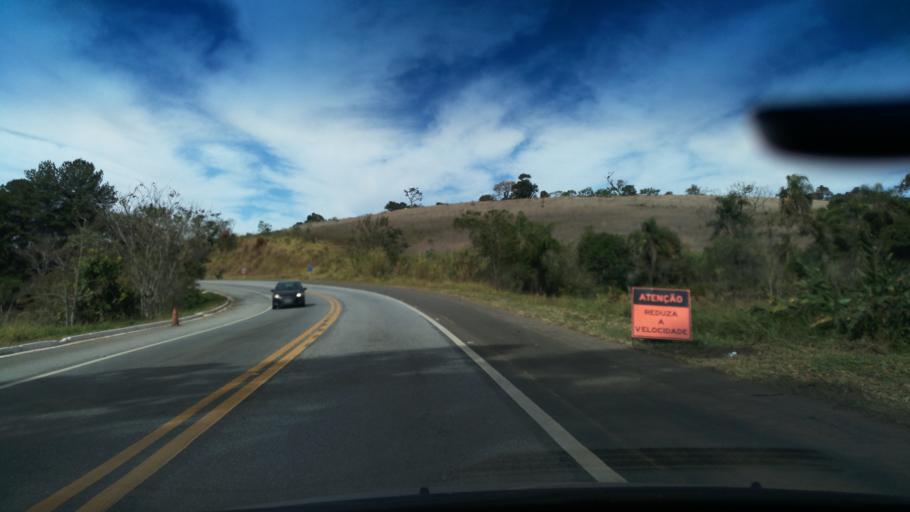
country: BR
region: Minas Gerais
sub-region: Borda Da Mata
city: Borda da Mata
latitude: -22.1444
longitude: -46.1315
